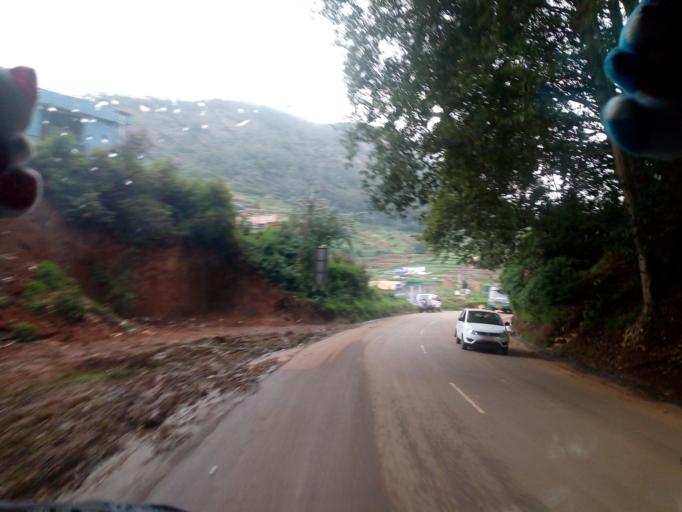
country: IN
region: Tamil Nadu
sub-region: Nilgiri
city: Ooty
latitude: 11.3994
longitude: 76.7172
